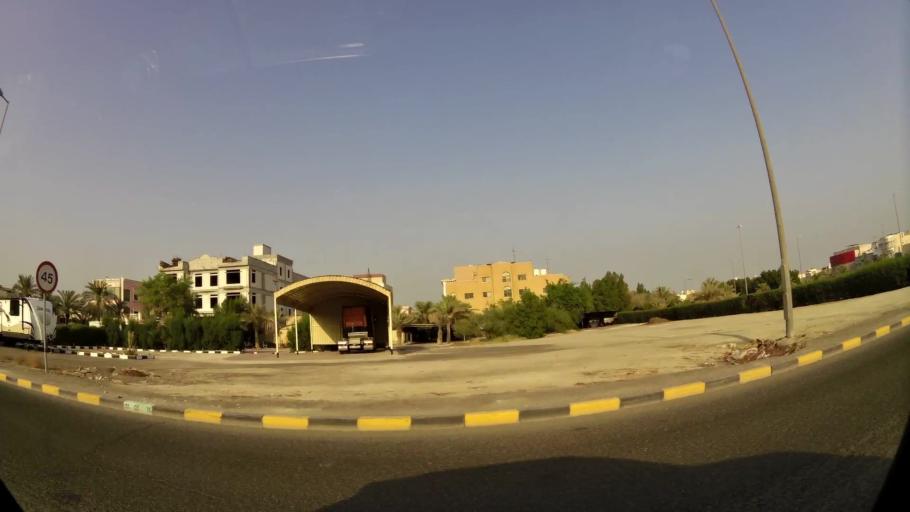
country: KW
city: Bayan
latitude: 29.3053
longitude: 48.0611
